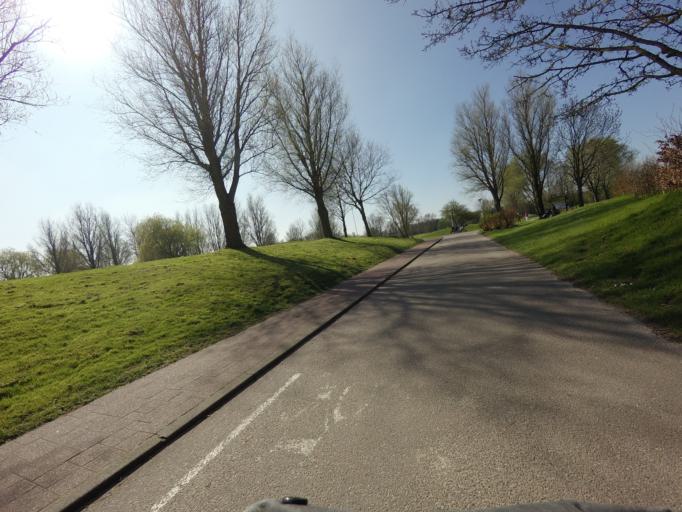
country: NL
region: North Holland
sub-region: Gemeente Heemstede
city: Heemstede
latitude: 52.3393
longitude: 4.6557
